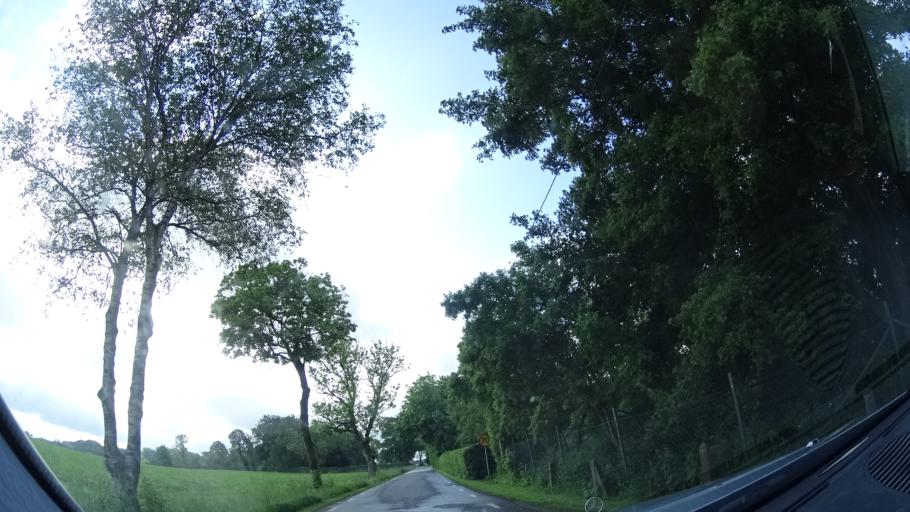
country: SE
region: Skane
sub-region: Eslovs Kommun
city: Stehag
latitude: 55.8957
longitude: 13.4156
